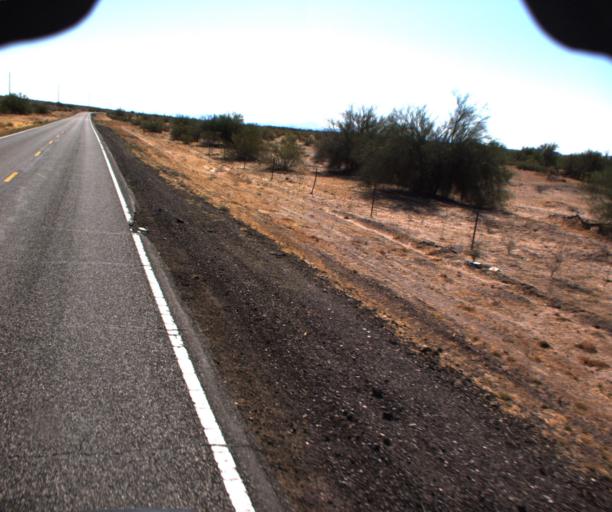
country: US
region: Arizona
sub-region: La Paz County
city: Parker
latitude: 33.9950
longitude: -114.1928
